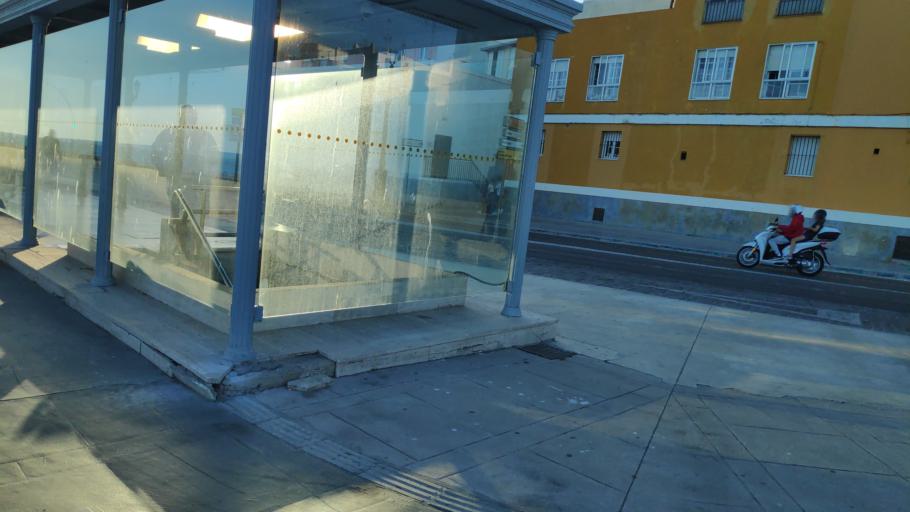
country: ES
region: Andalusia
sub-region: Provincia de Cadiz
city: Cadiz
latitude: 36.5288
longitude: -6.2979
